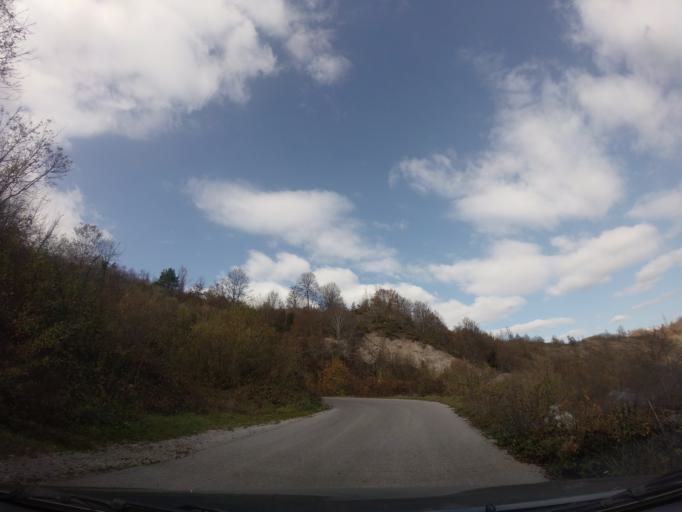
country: HR
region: Karlovacka
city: Plaski
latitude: 45.1969
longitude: 15.4275
